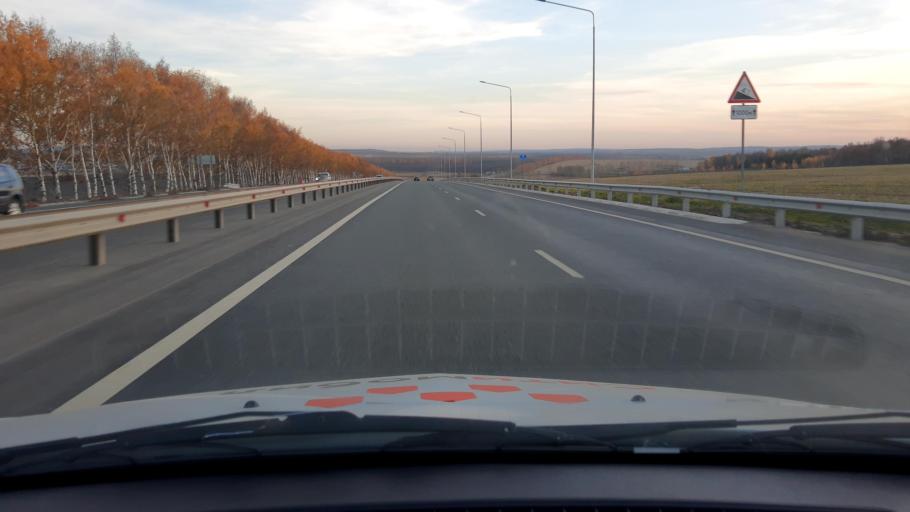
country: RU
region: Bashkortostan
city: Karmaskaly
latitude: 54.3727
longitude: 55.9171
